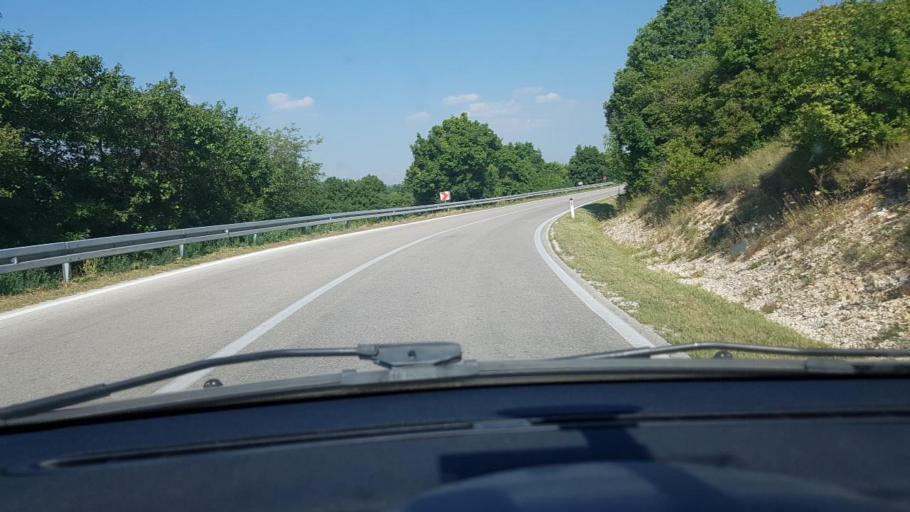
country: BA
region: Federation of Bosnia and Herzegovina
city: Bila
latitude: 43.8653
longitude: 16.8861
